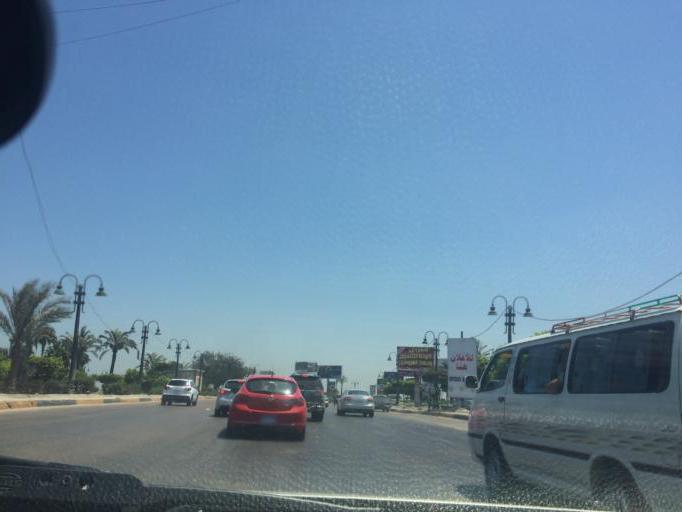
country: EG
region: Alexandria
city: Alexandria
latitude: 31.1685
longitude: 29.9347
